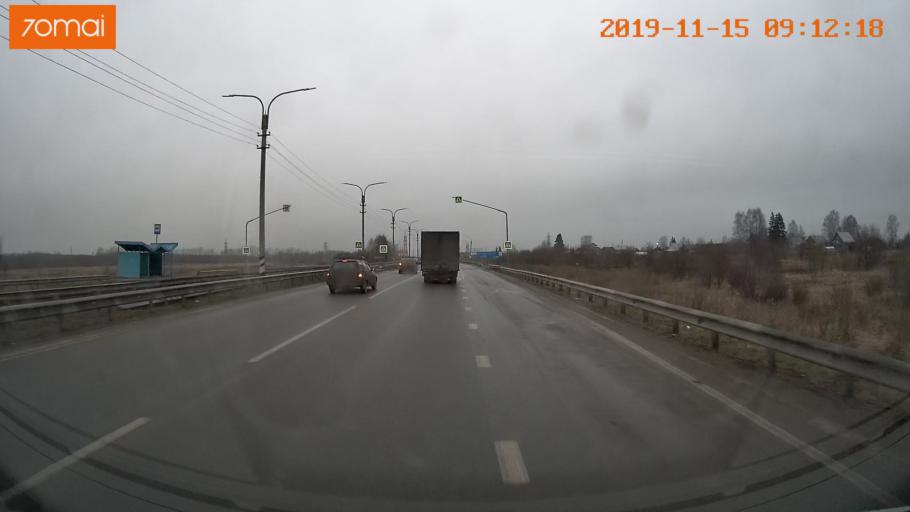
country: RU
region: Vologda
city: Tonshalovo
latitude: 59.2067
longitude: 37.9384
